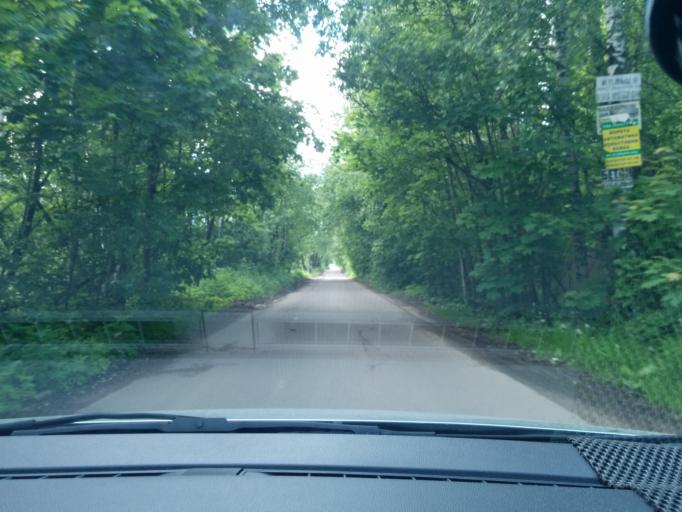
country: RU
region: Moskovskaya
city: Lugovaya
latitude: 56.0522
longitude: 37.4830
